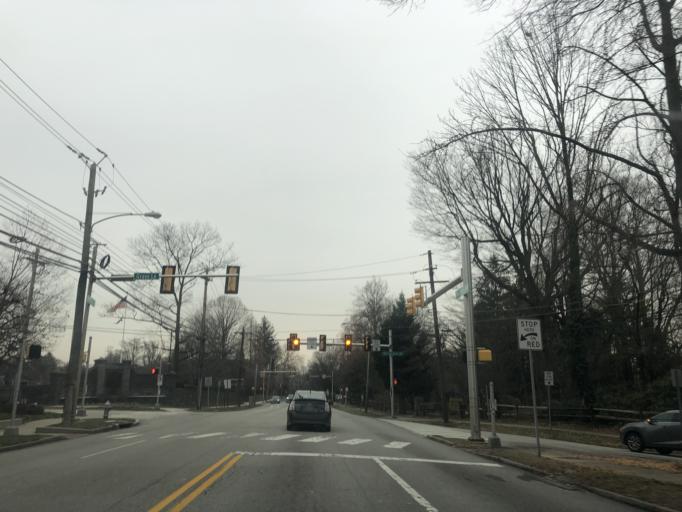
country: US
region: Pennsylvania
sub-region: Montgomery County
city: Bryn Mawr
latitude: 40.0159
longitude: -75.3007
